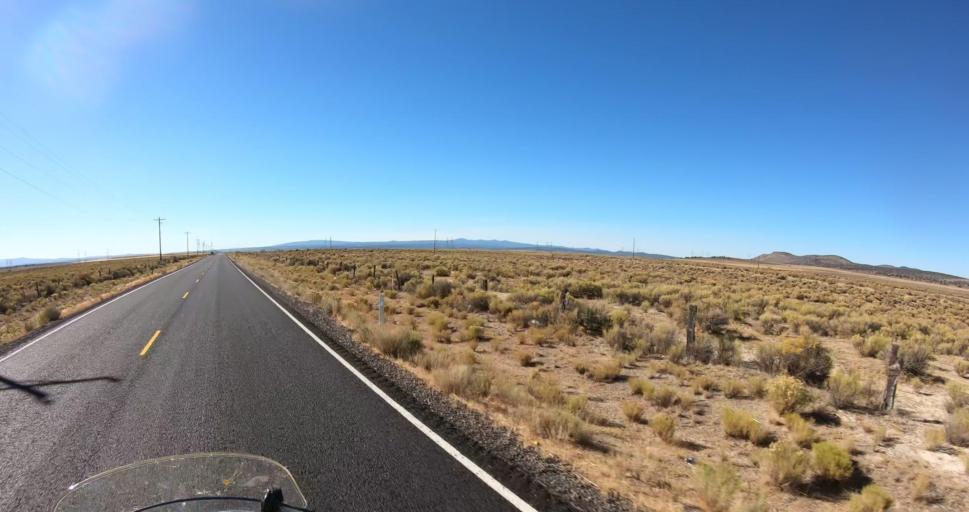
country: US
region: Oregon
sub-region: Deschutes County
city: La Pine
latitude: 43.1300
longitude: -120.9313
